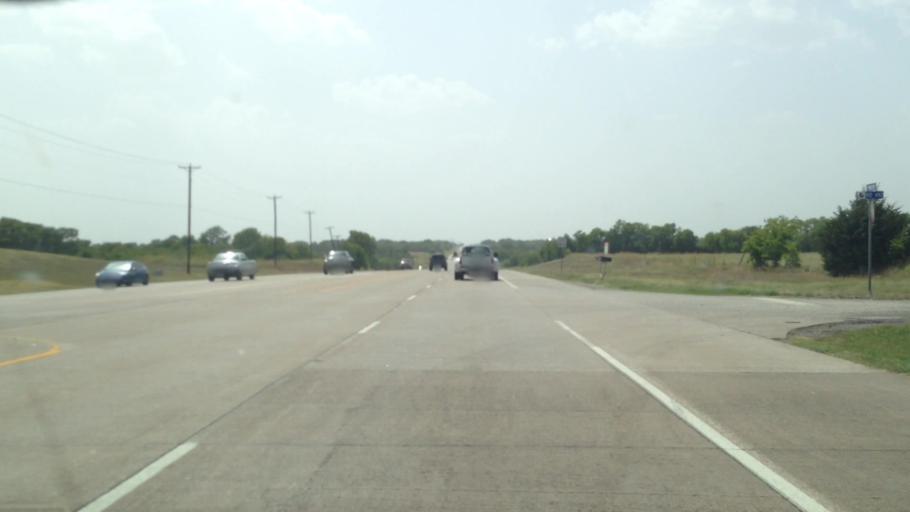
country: US
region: Texas
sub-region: Collin County
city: Princeton
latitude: 33.1682
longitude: -96.4638
